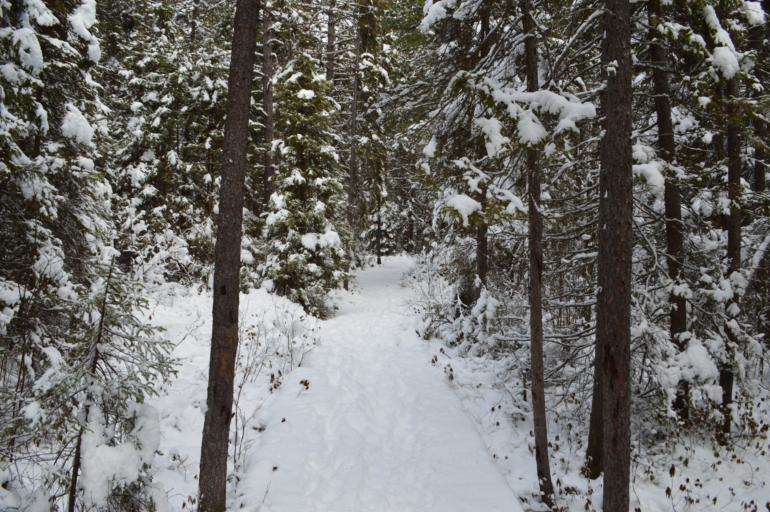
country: CA
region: Ontario
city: Bancroft
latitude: 45.5911
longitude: -78.3715
